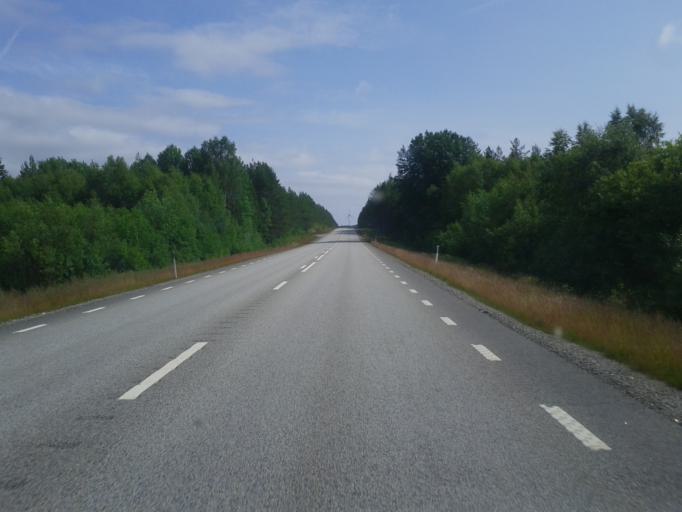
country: SE
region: Vaesterbotten
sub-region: Robertsfors Kommun
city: Robertsfors
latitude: 64.1753
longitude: 20.9500
